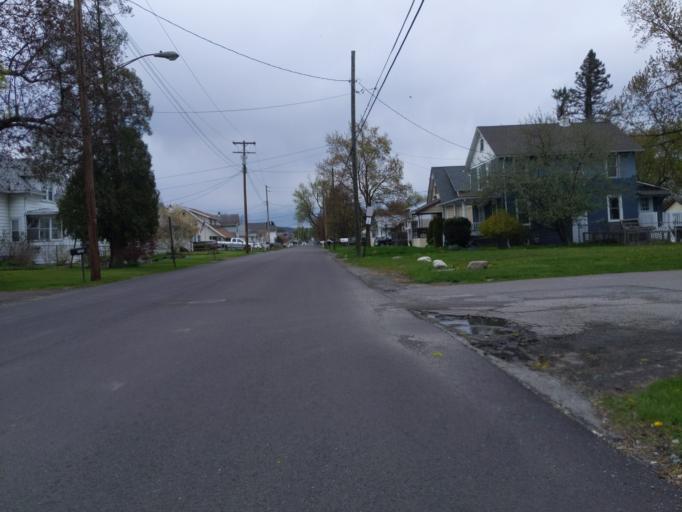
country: US
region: New York
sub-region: Chemung County
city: Southport
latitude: 42.0609
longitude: -76.8110
